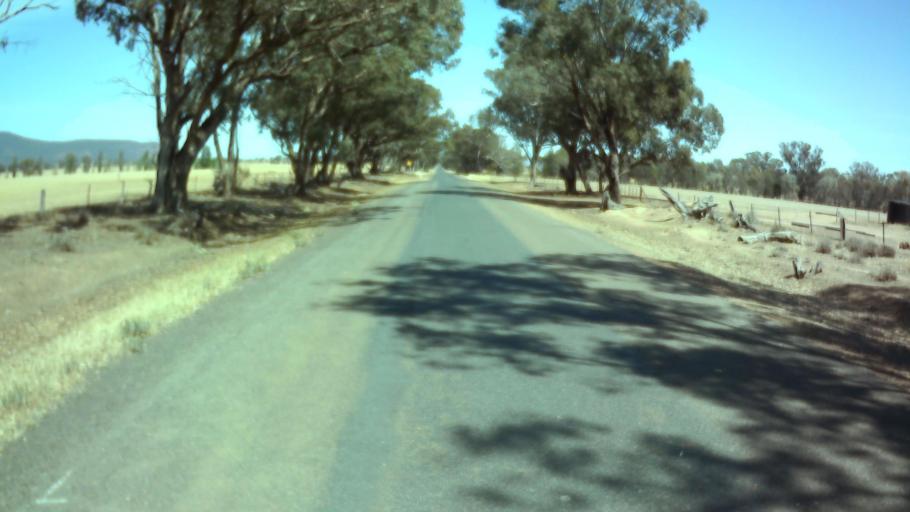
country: AU
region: New South Wales
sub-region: Weddin
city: Grenfell
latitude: -33.8659
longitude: 148.0516
